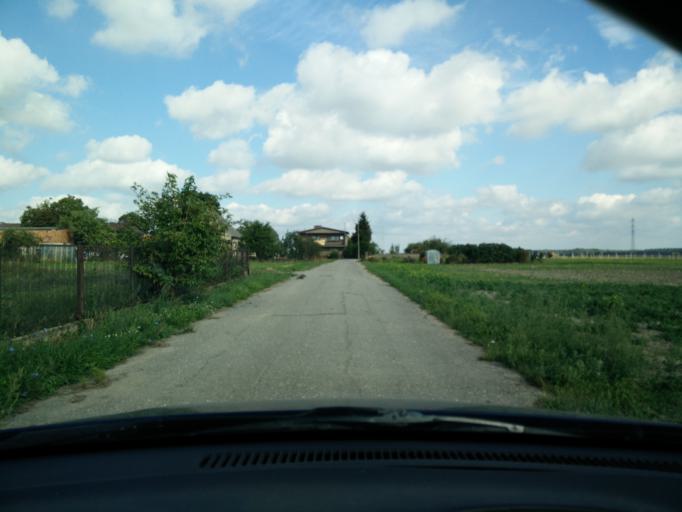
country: PL
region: Greater Poland Voivodeship
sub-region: Powiat sredzki
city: Dominowo
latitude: 52.2878
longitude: 17.3877
